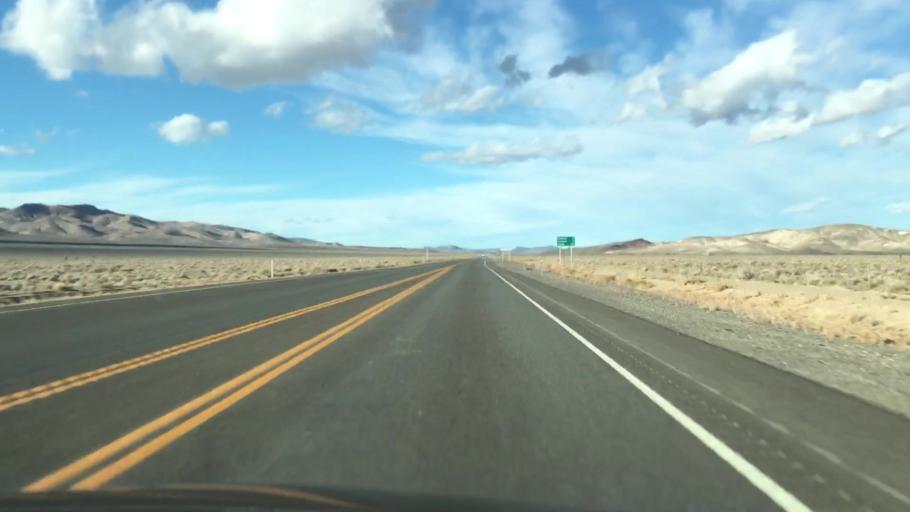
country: US
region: Nevada
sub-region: Esmeralda County
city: Goldfield
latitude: 37.5044
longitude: -117.1851
